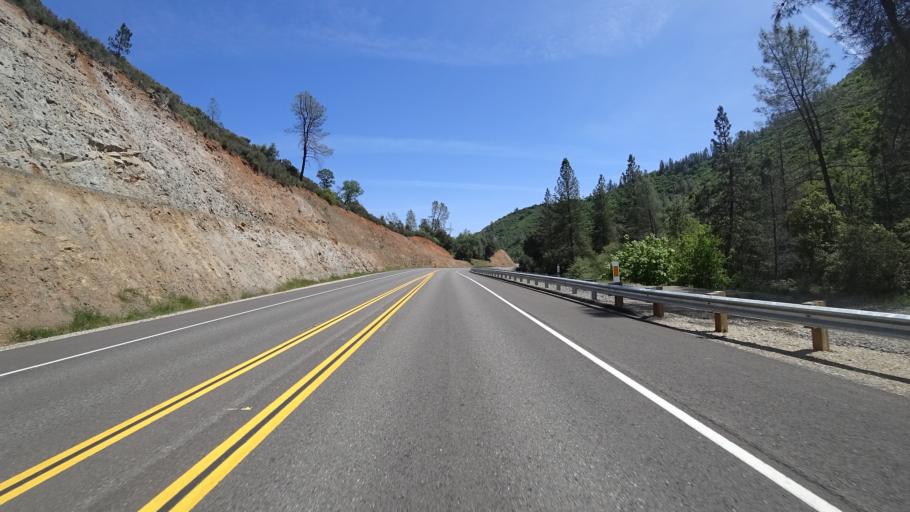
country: US
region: California
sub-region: Trinity County
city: Lewiston
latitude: 40.6734
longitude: -122.6638
